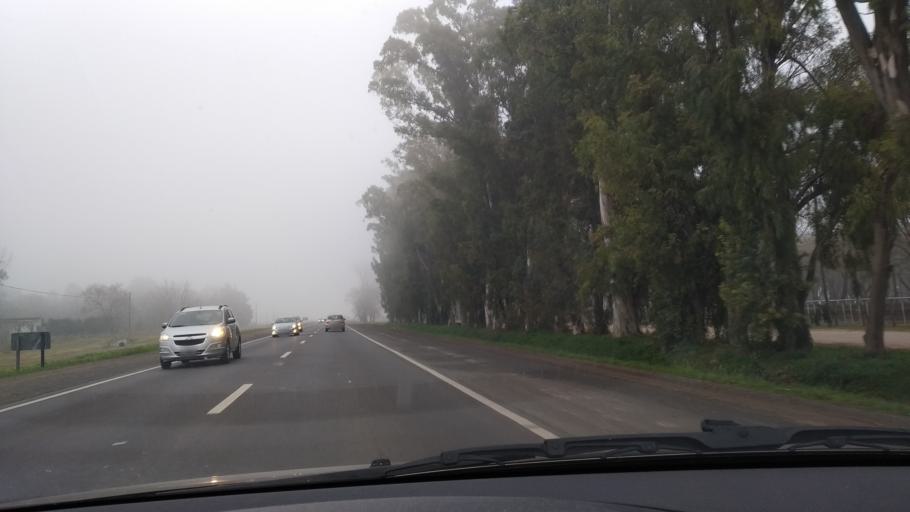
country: AR
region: Buenos Aires
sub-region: Partido de Azul
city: Azul
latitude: -36.8121
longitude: -59.8643
